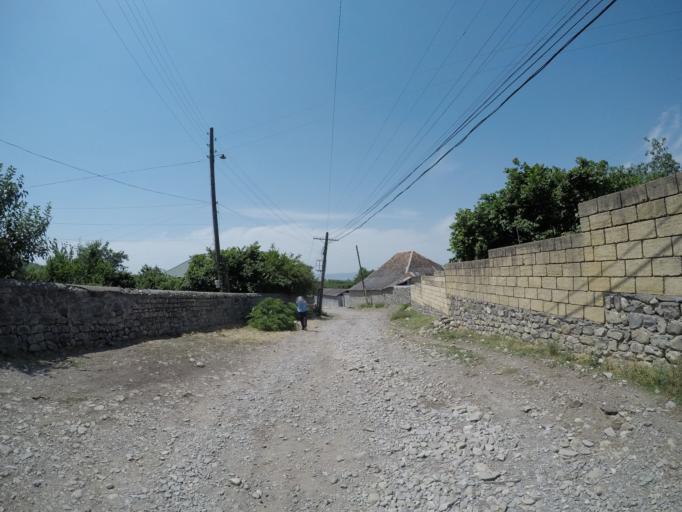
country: AZ
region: Qakh Rayon
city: Cinarli
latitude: 41.4843
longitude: 46.8498
